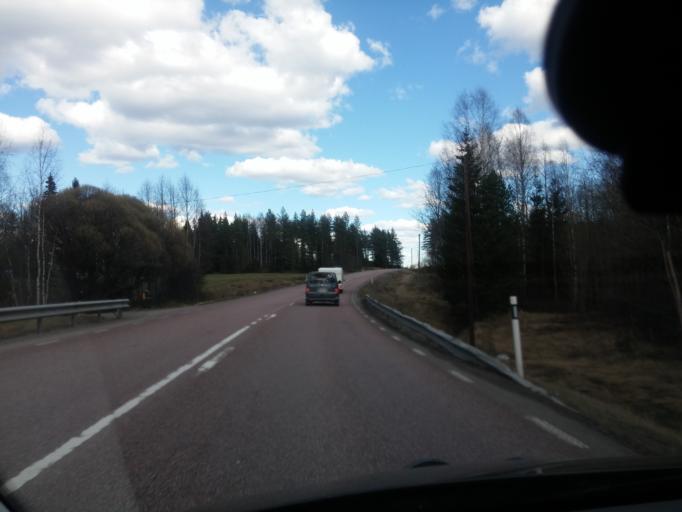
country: SE
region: Gaevleborg
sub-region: Ljusdals Kommun
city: Farila
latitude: 61.8125
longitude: 15.9590
